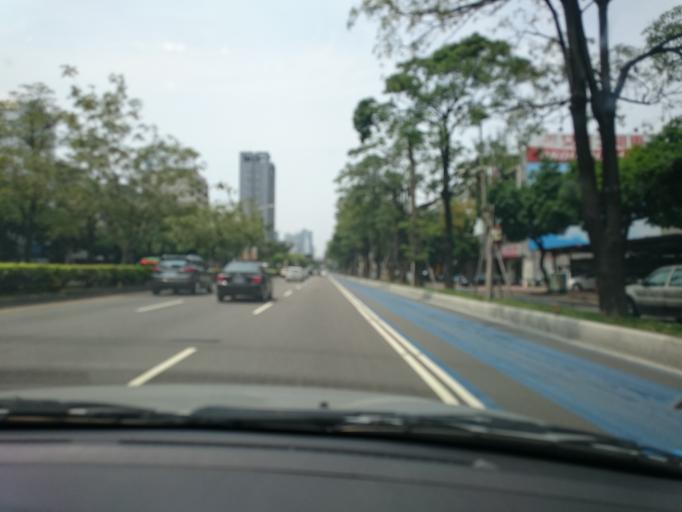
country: TW
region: Taiwan
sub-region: Taichung City
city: Taichung
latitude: 24.1596
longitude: 120.6554
